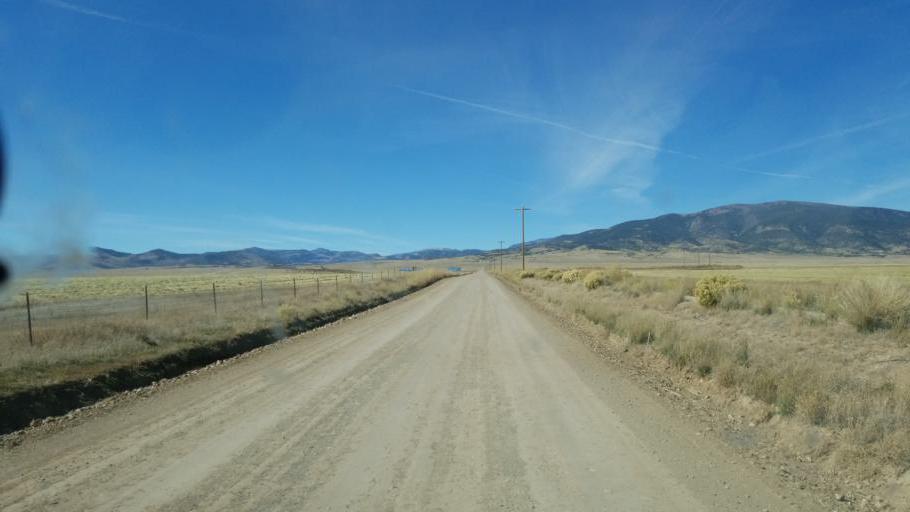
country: US
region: Colorado
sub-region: Rio Grande County
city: Monte Vista
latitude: 37.4011
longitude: -106.1334
